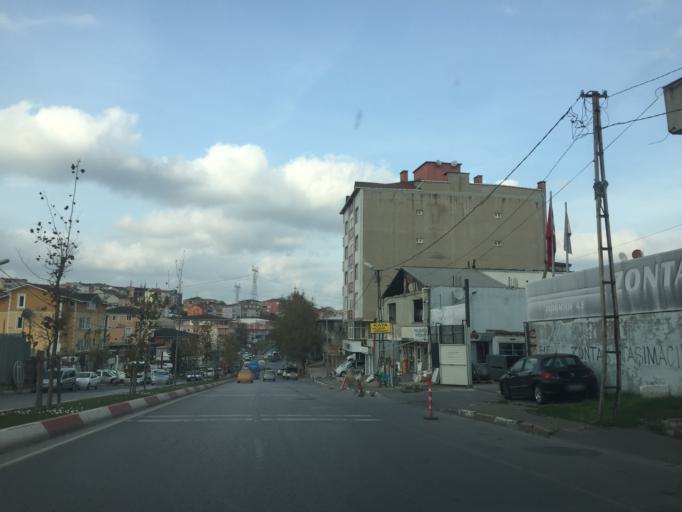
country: TR
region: Istanbul
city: Sultanbeyli
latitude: 40.9460
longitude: 29.2992
